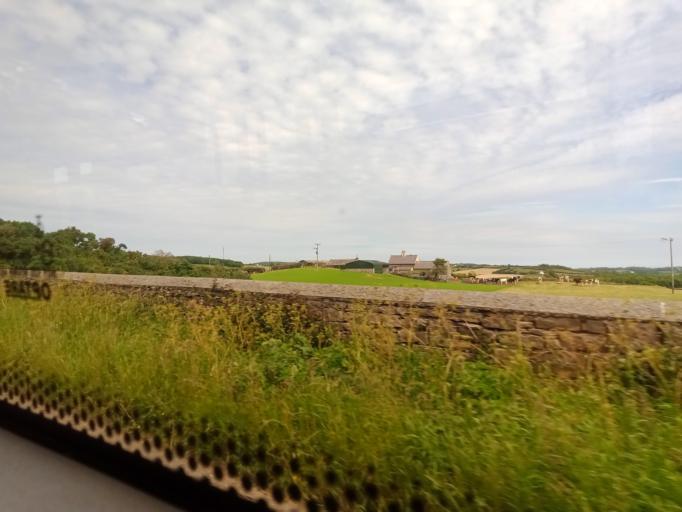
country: GB
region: Wales
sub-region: Anglesey
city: Beaumaris
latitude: 53.2804
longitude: -4.1252
